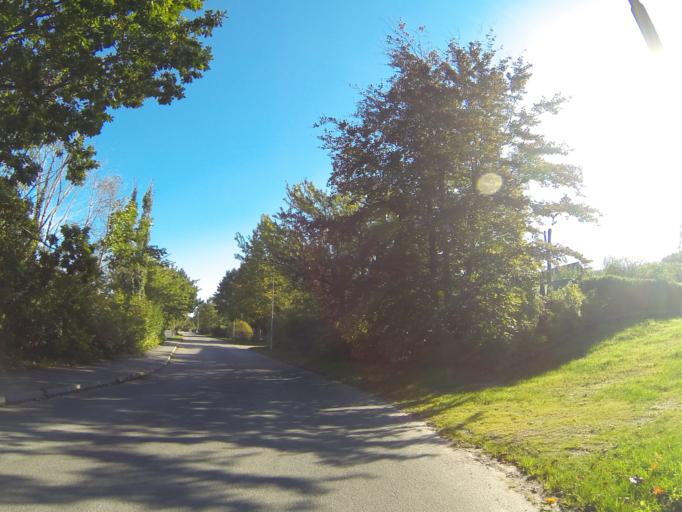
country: SE
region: Skane
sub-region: Lunds Kommun
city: Genarp
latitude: 55.7103
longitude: 13.3282
